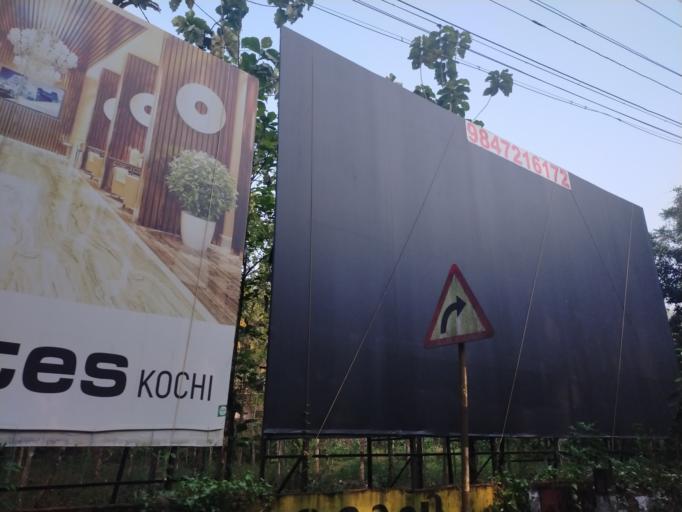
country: IN
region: Kerala
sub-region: Kottayam
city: Vaikam
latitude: 9.7540
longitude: 76.5041
